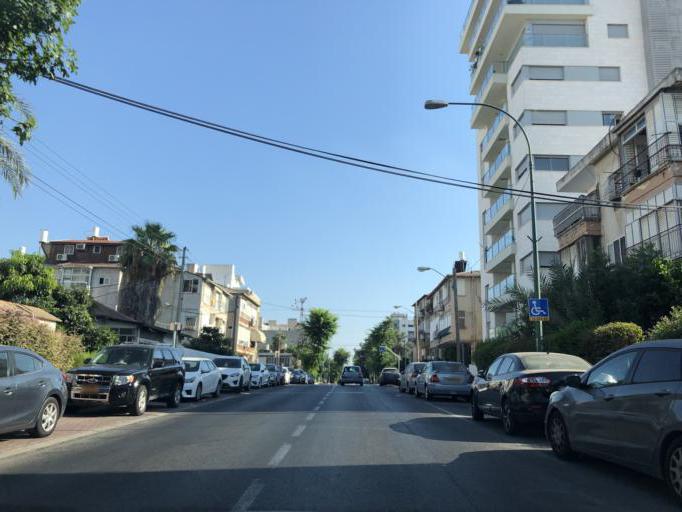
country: IL
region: Tel Aviv
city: Giv`atayim
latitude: 32.0693
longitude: 34.8246
